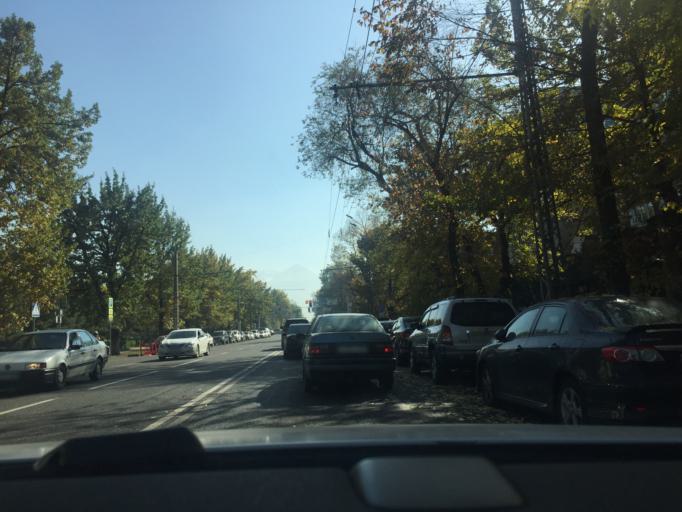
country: KZ
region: Almaty Qalasy
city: Almaty
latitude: 43.2411
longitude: 76.9038
